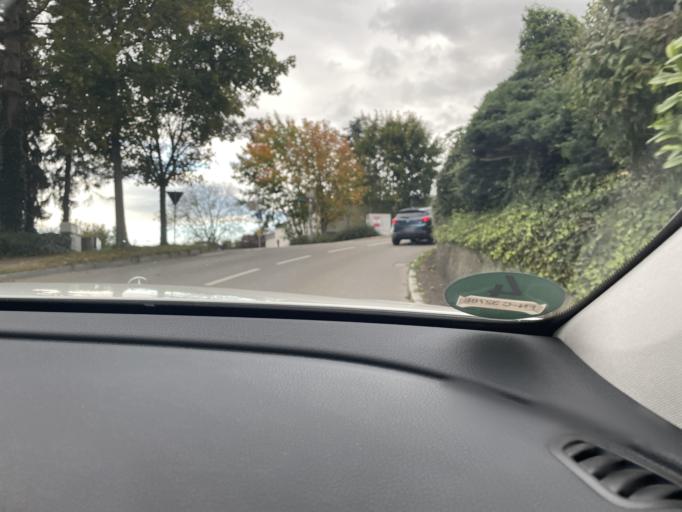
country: DE
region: Baden-Wuerttemberg
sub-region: Tuebingen Region
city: Markdorf
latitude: 47.7242
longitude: 9.3962
